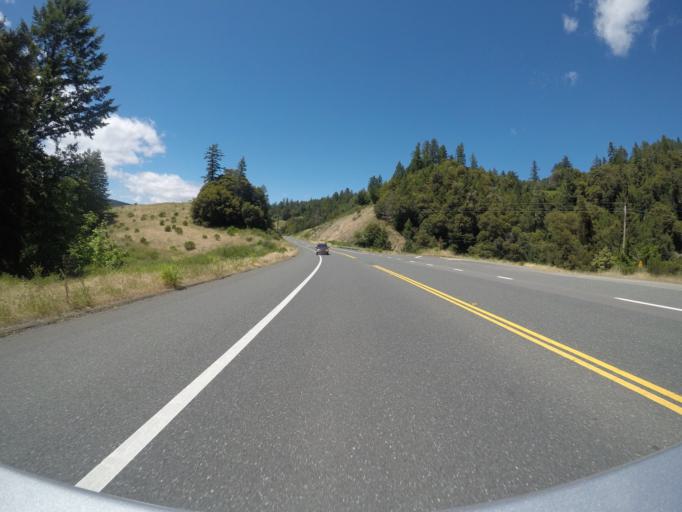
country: US
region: California
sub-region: Humboldt County
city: Redway
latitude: 39.9288
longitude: -123.7614
